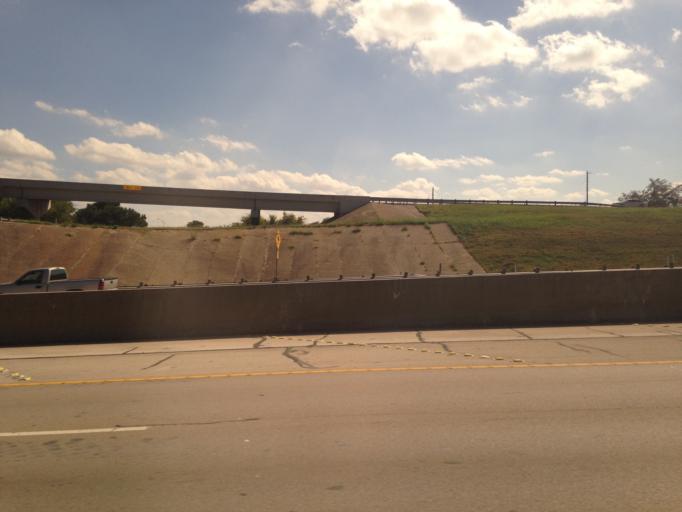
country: US
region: Texas
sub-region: Tarrant County
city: White Settlement
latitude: 32.7384
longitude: -97.4826
